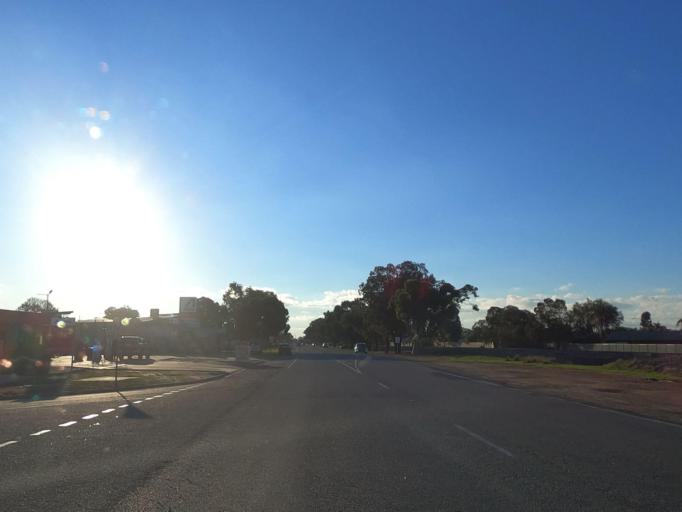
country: AU
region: Victoria
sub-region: Swan Hill
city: Swan Hill
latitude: -35.3329
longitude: 143.5585
